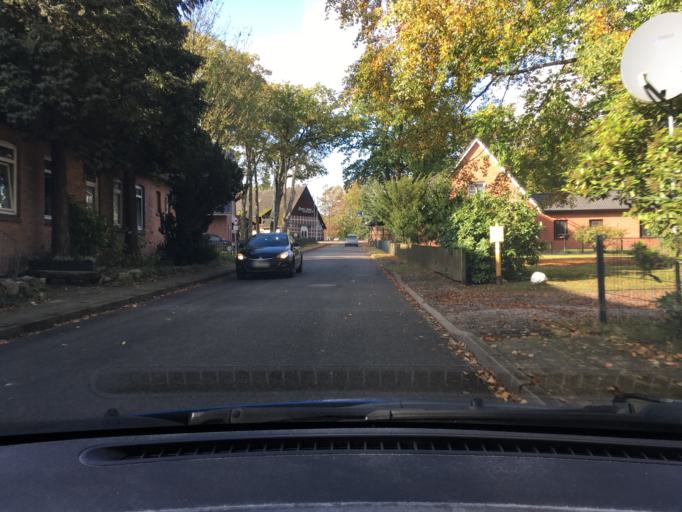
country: DE
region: Lower Saxony
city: Kakenstorf
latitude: 53.3194
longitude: 9.7916
